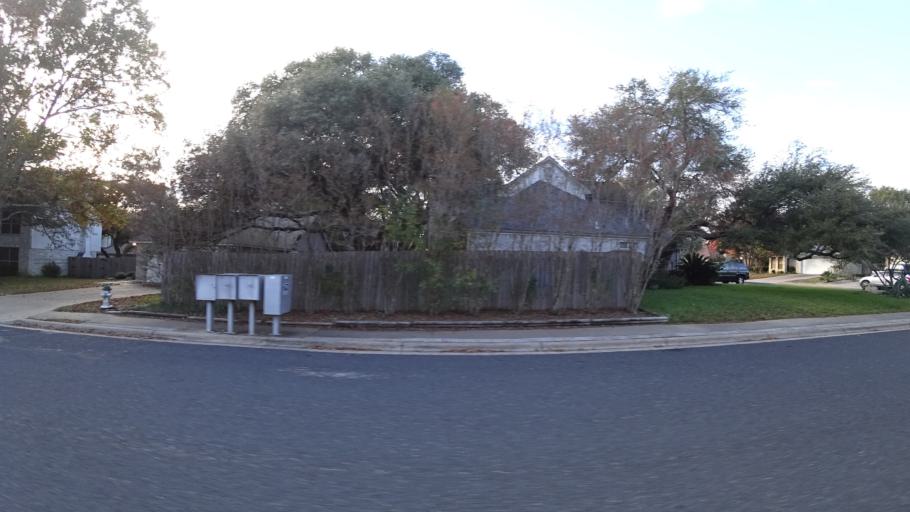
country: US
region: Texas
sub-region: Williamson County
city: Brushy Creek
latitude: 30.4916
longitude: -97.7385
